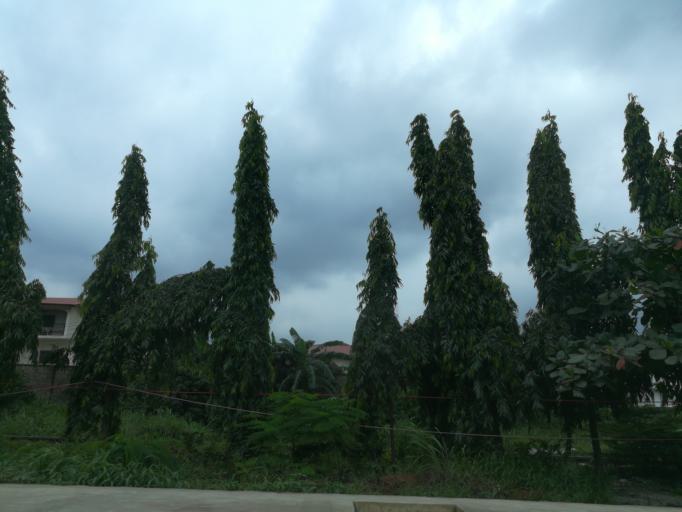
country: NG
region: Lagos
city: Ikeja
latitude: 6.5862
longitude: 3.3395
